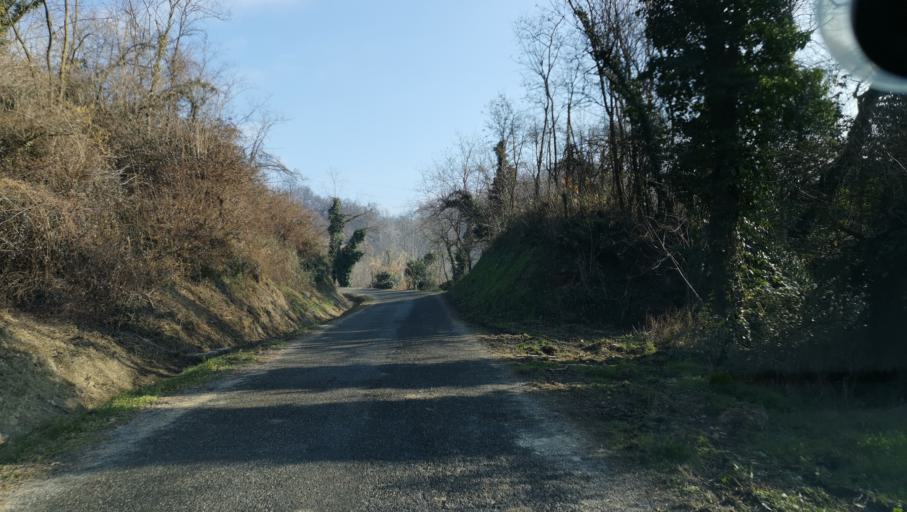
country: IT
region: Piedmont
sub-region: Provincia di Torino
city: Rivalba
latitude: 45.1374
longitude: 7.8870
